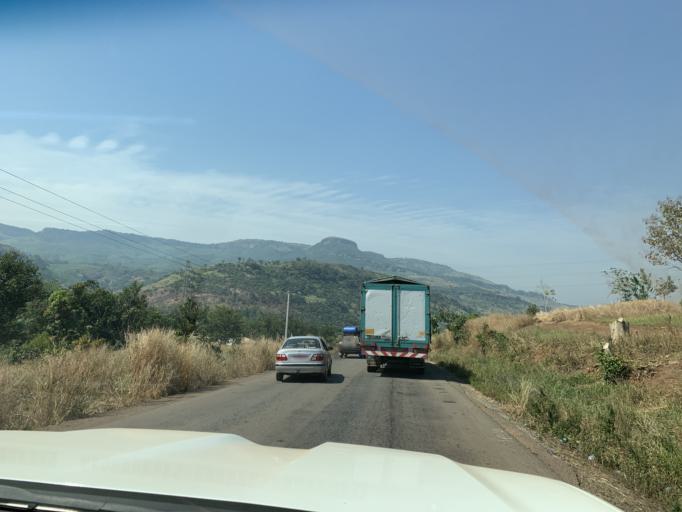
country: GN
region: Mamou
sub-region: Mamou Prefecture
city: Mamou
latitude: 10.1934
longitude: -12.4595
